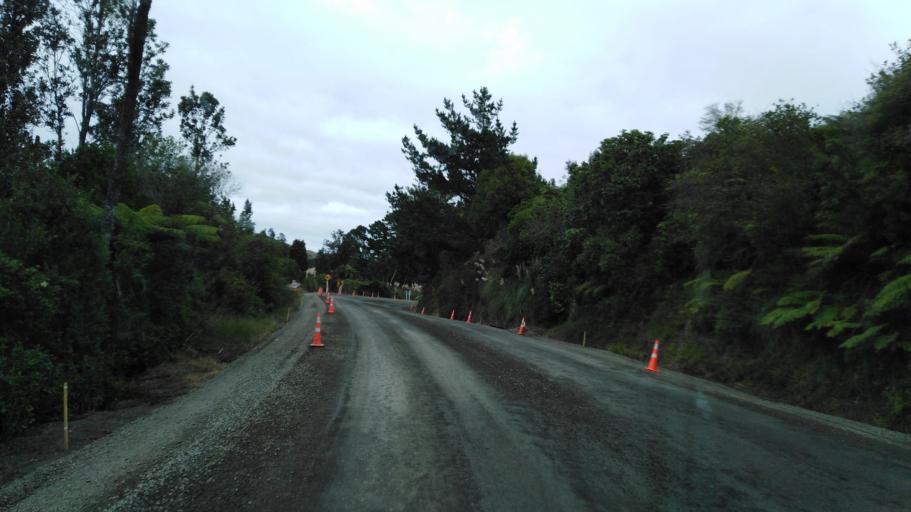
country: NZ
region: Bay of Plenty
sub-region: Western Bay of Plenty District
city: Waihi Beach
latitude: -37.4114
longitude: 175.9244
